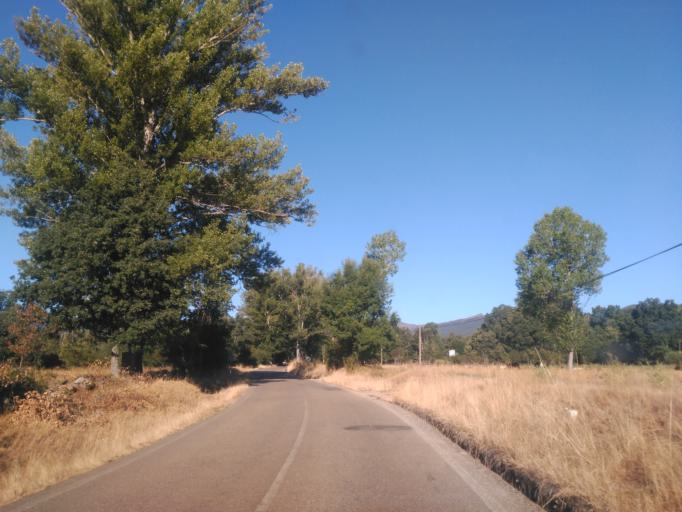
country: ES
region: Castille and Leon
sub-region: Provincia de Zamora
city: Galende
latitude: 42.0877
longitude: -6.6736
